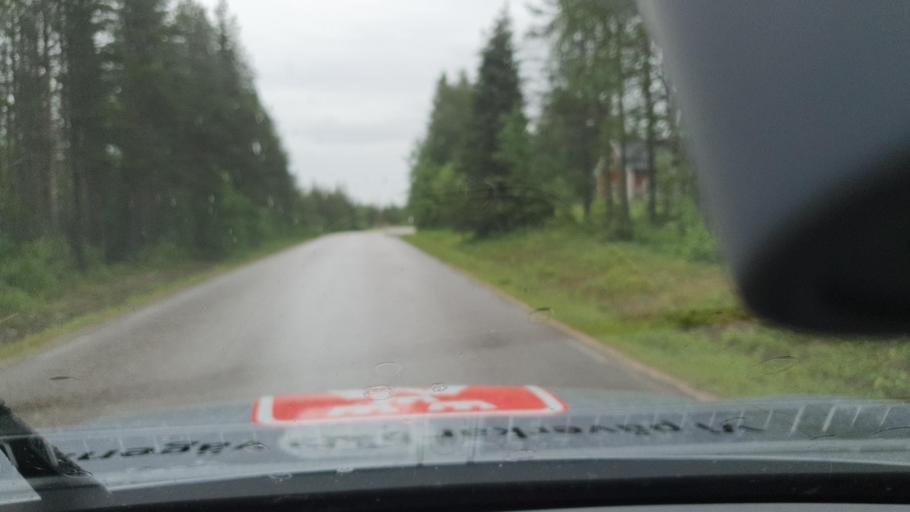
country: SE
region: Norrbotten
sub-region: Pajala Kommun
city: Pajala
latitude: 66.8309
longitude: 23.1163
